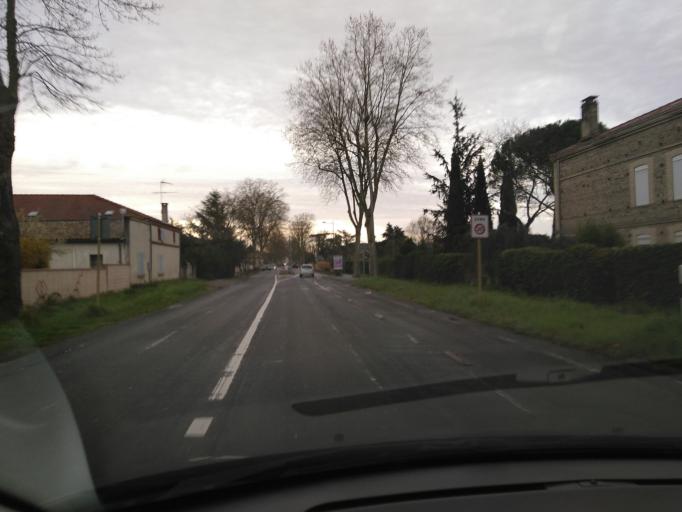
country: FR
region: Midi-Pyrenees
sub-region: Departement de la Haute-Garonne
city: Castelnau-d'Estretefonds
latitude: 43.7874
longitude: 1.3513
